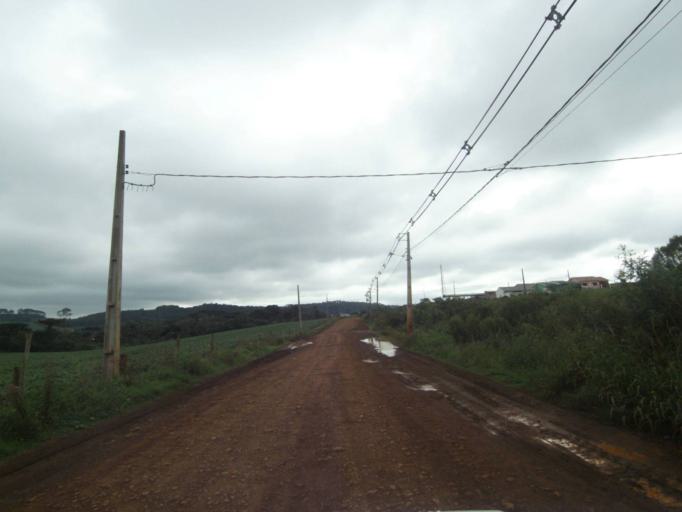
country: BR
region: Parana
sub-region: Pitanga
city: Pitanga
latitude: -24.9408
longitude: -51.8781
